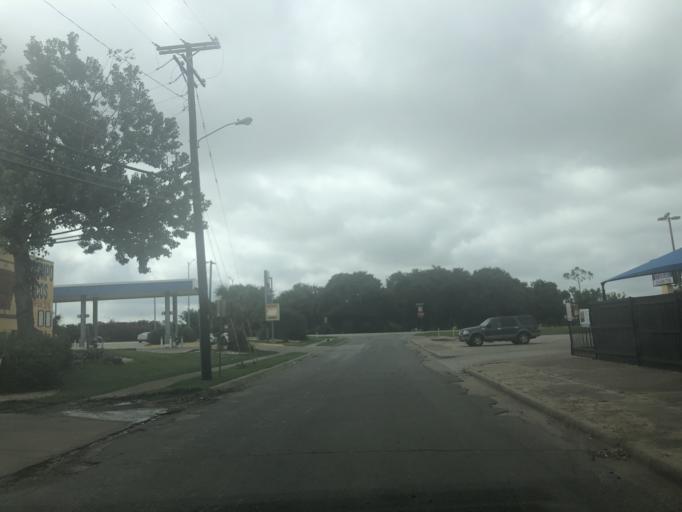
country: US
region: Texas
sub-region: Dallas County
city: University Park
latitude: 32.8567
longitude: -96.8654
